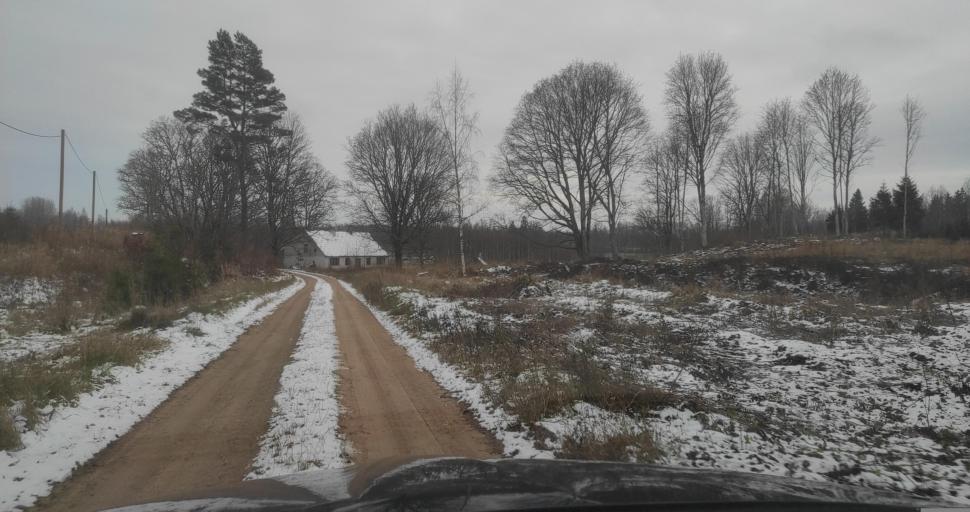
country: LV
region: Alsunga
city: Alsunga
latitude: 56.9591
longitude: 21.6424
